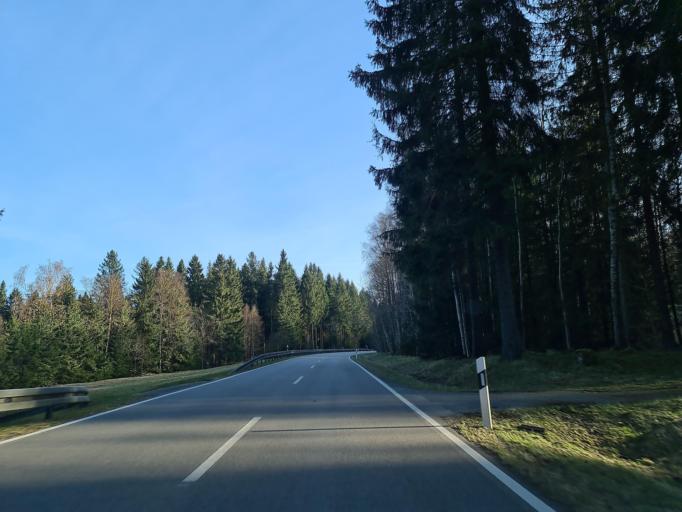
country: DE
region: Saxony
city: Hammerbrucke
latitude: 50.4295
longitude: 12.4013
